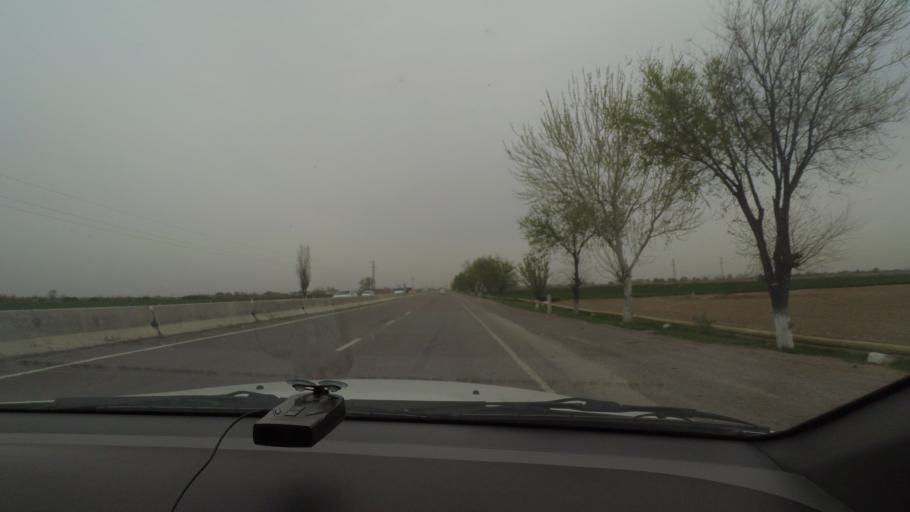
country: KZ
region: Ongtustik Qazaqstan
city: Myrzakent
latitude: 40.5565
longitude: 68.3907
